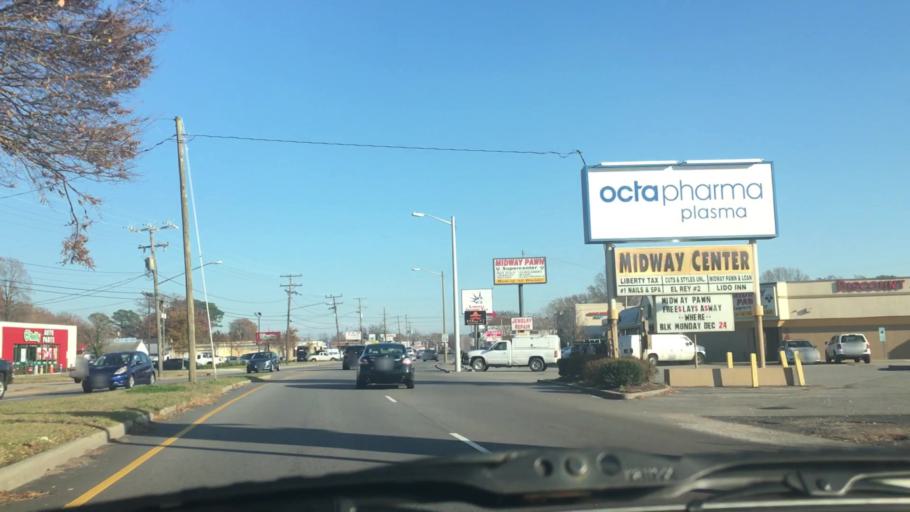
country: US
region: Virginia
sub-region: City of Norfolk
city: Norfolk
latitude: 36.9152
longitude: -76.2495
